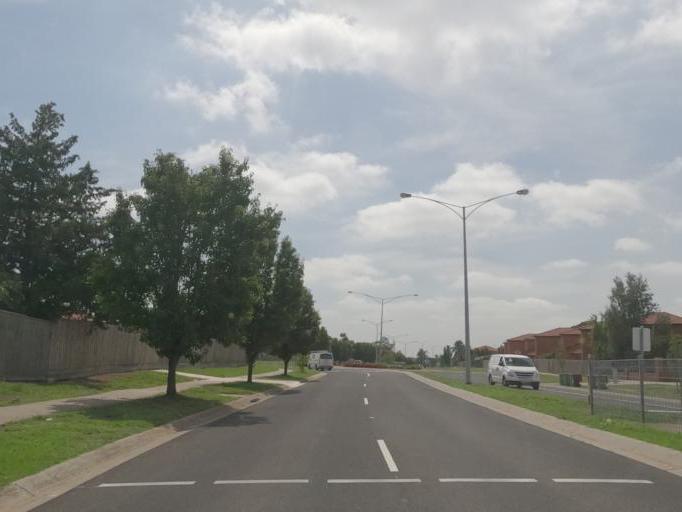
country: AU
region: Victoria
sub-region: Hume
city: Attwood
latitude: -37.6520
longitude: 144.8890
